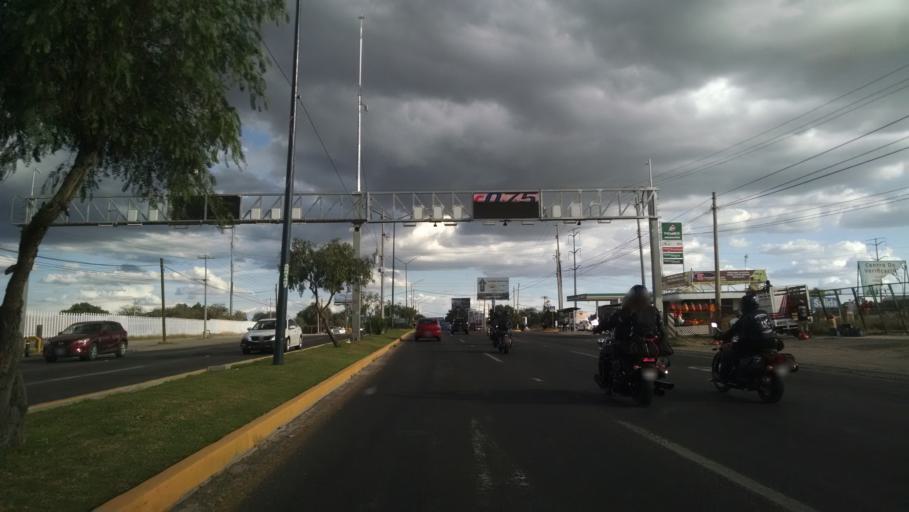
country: MX
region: Guanajuato
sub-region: Leon
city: Fraccionamiento Paraiso Real
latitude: 21.0753
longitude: -101.6021
